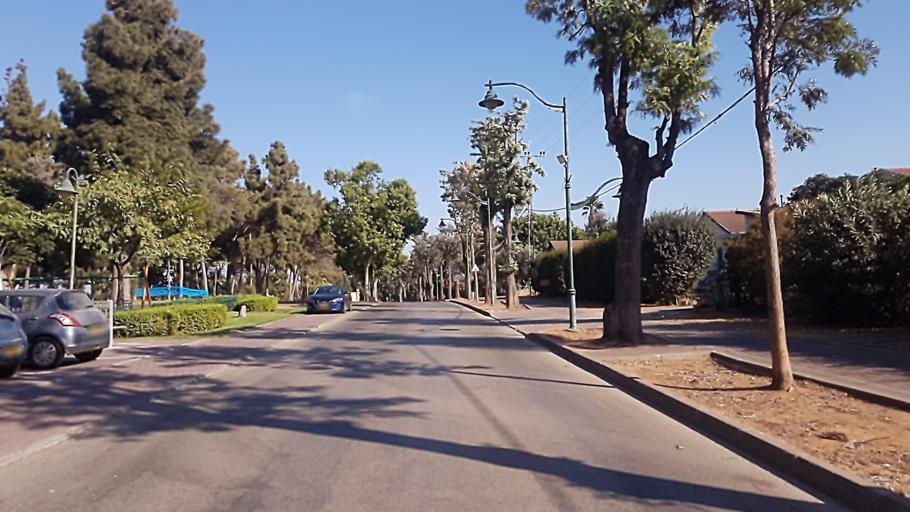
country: IL
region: Central District
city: Kfar Saba
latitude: 32.2103
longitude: 34.8993
